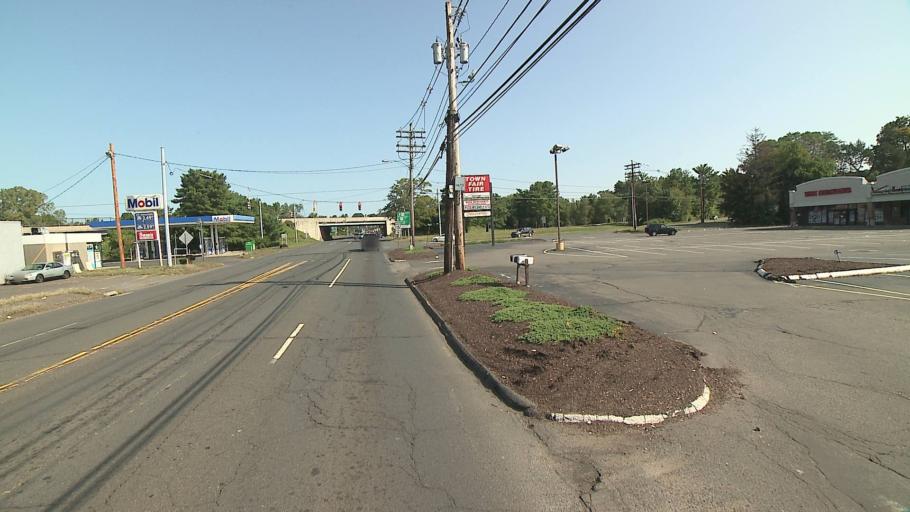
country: US
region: Connecticut
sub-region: New Haven County
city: Wallingford
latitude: 41.4899
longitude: -72.8095
